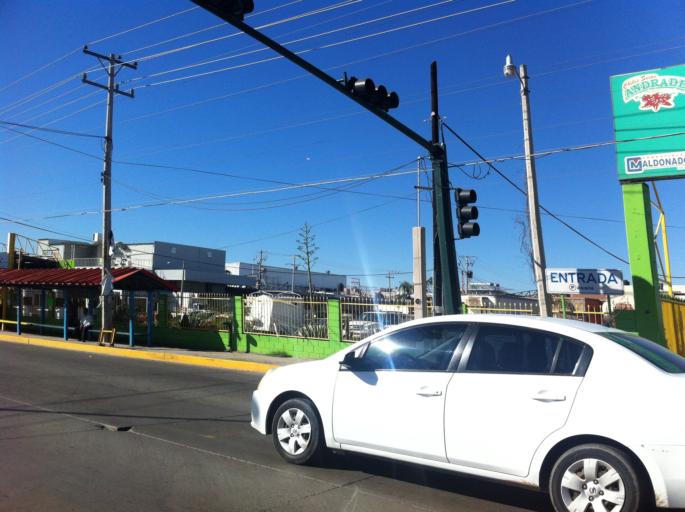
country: MX
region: Sonora
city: Hermosillo
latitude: 29.1149
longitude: -110.9925
